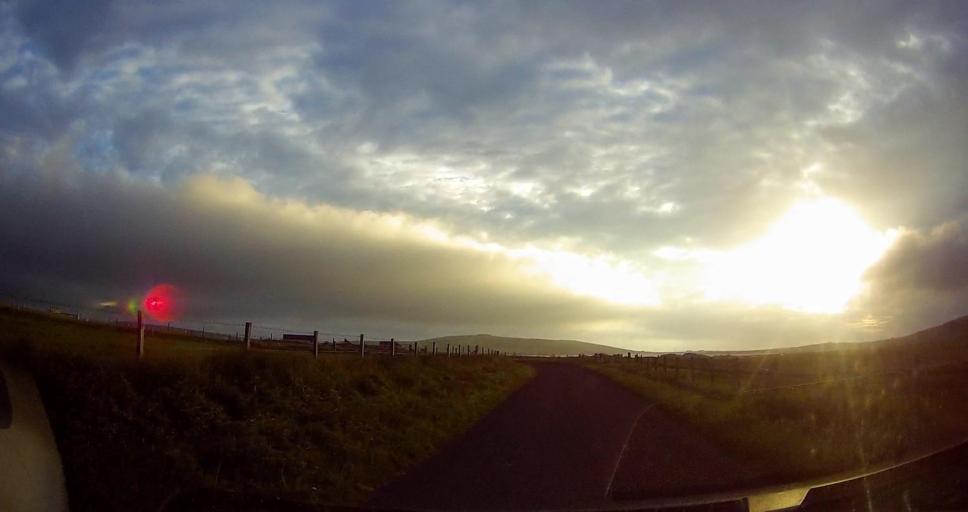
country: GB
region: Scotland
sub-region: Orkney Islands
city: Stromness
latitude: 59.1072
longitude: -3.2397
